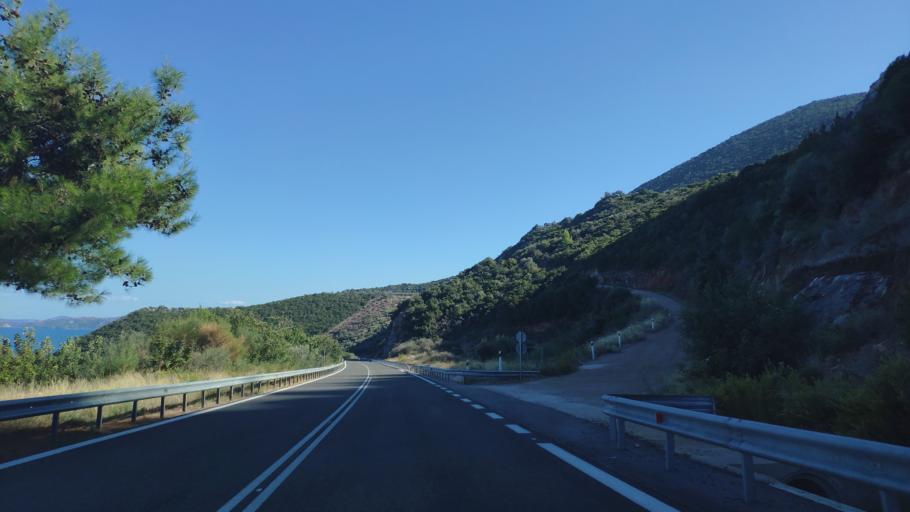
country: GR
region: Peloponnese
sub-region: Nomos Argolidos
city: Didyma
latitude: 37.5557
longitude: 23.2607
